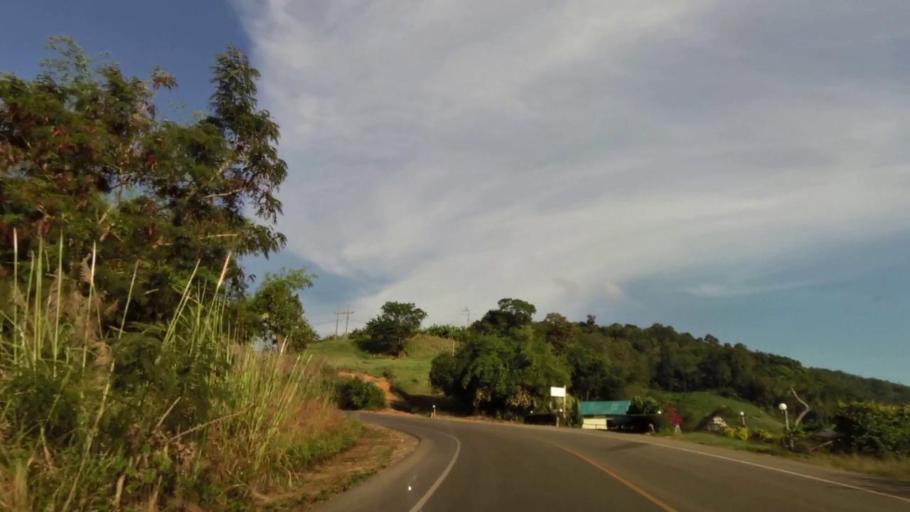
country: TH
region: Chiang Rai
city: Khun Tan
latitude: 19.8583
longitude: 100.4303
